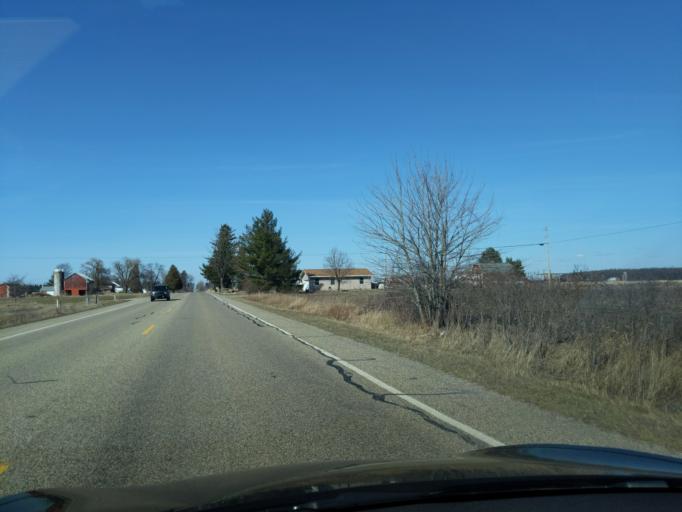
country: US
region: Michigan
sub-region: Ionia County
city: Lake Odessa
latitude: 42.8349
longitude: -85.1338
